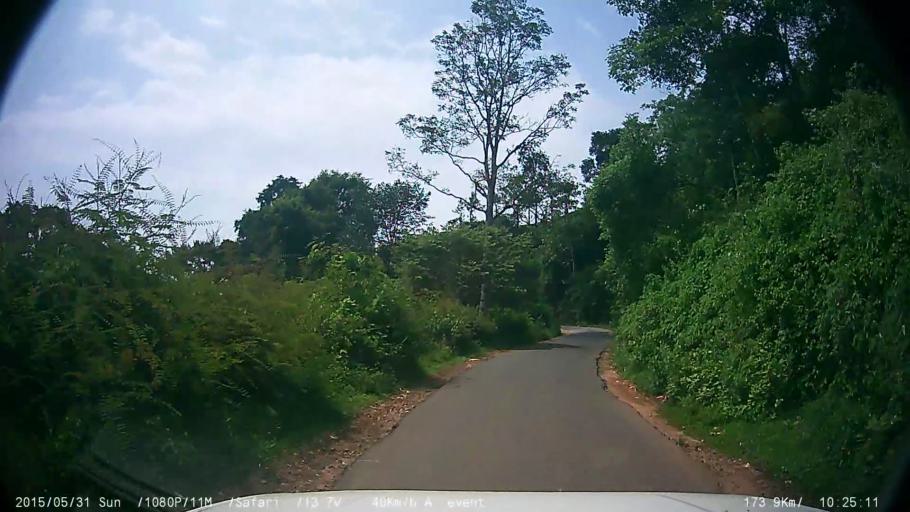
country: IN
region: Kerala
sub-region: Wayanad
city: Kalpetta
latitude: 11.5309
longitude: 76.1387
